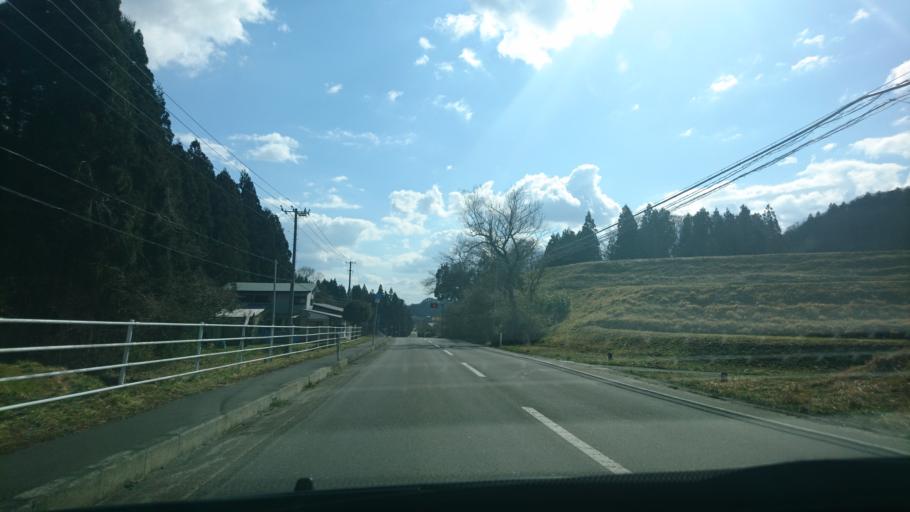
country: JP
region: Iwate
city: Kitakami
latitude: 39.2516
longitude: 141.2071
